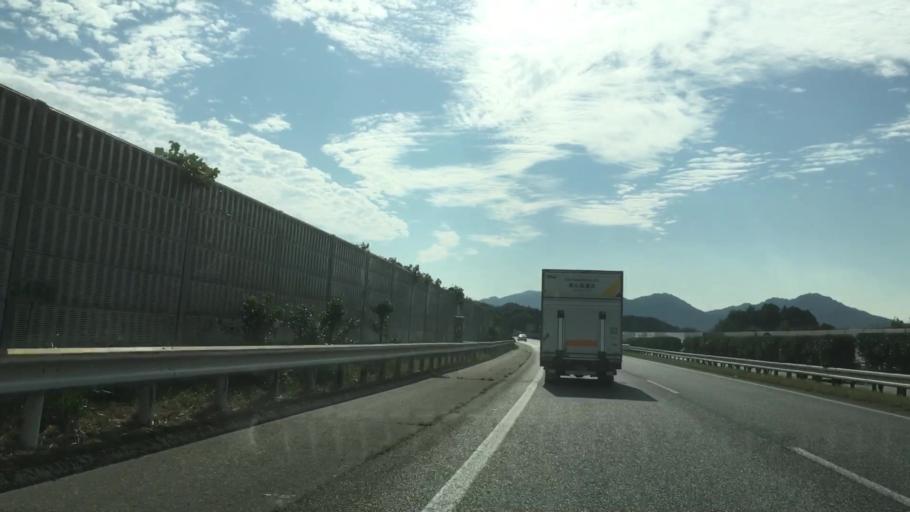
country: JP
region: Yamaguchi
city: Yanai
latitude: 34.0805
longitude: 132.0754
